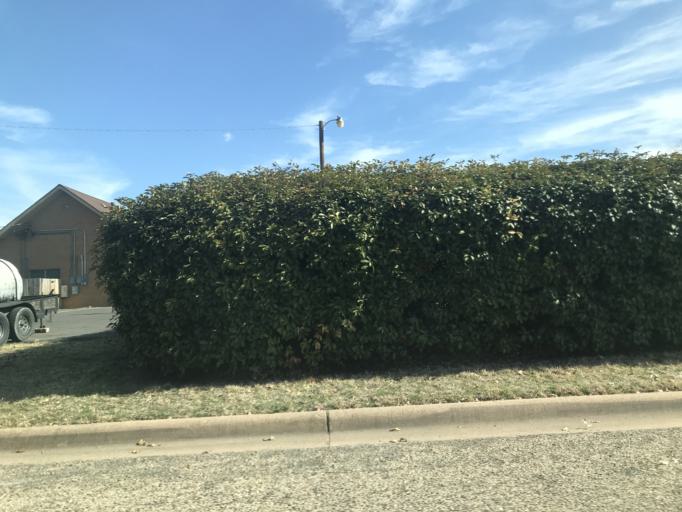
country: US
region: Texas
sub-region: Taylor County
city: Abilene
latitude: 32.4128
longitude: -99.7617
